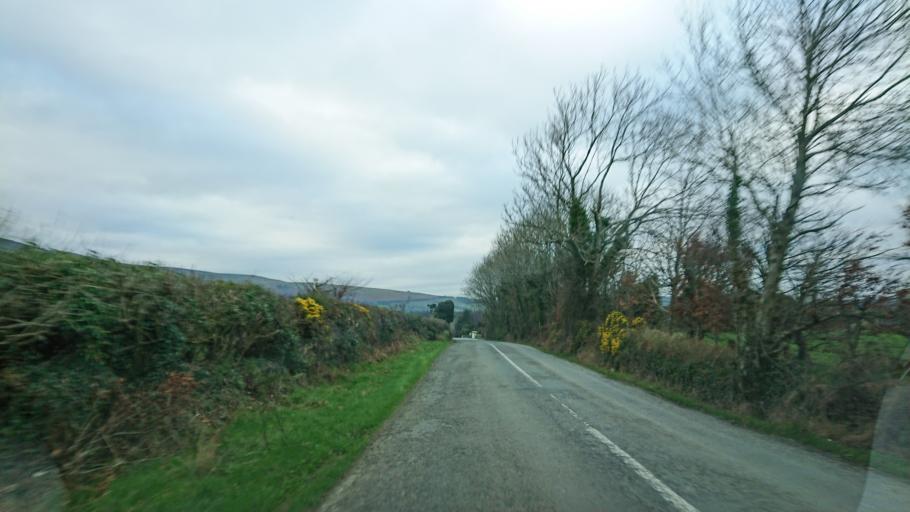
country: IE
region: Munster
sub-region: South Tipperary
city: Cluain Meala
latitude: 52.3213
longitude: -7.5656
